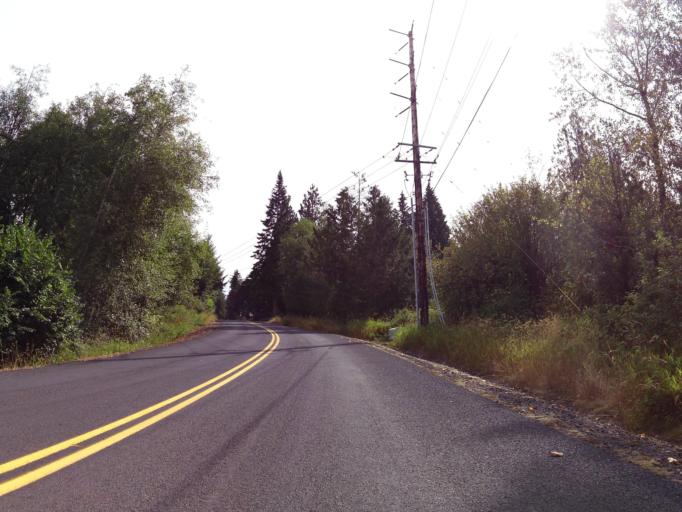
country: US
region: Washington
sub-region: Cowlitz County
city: Castle Rock
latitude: 46.3152
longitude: -122.9249
